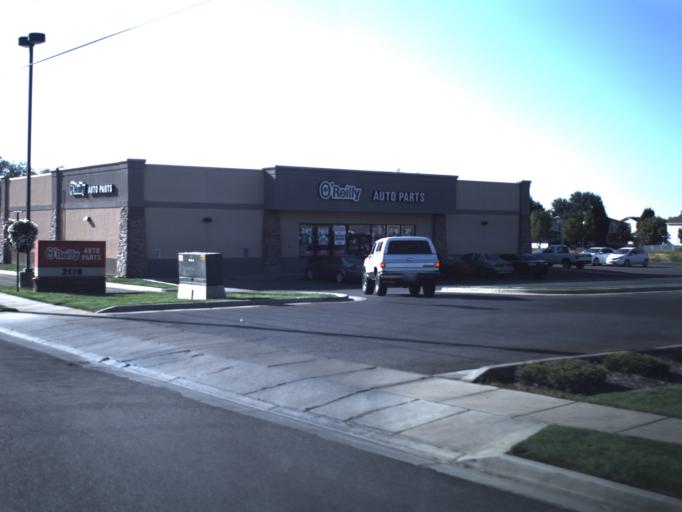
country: US
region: Utah
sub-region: Davis County
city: Clinton
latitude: 41.1399
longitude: -112.0675
